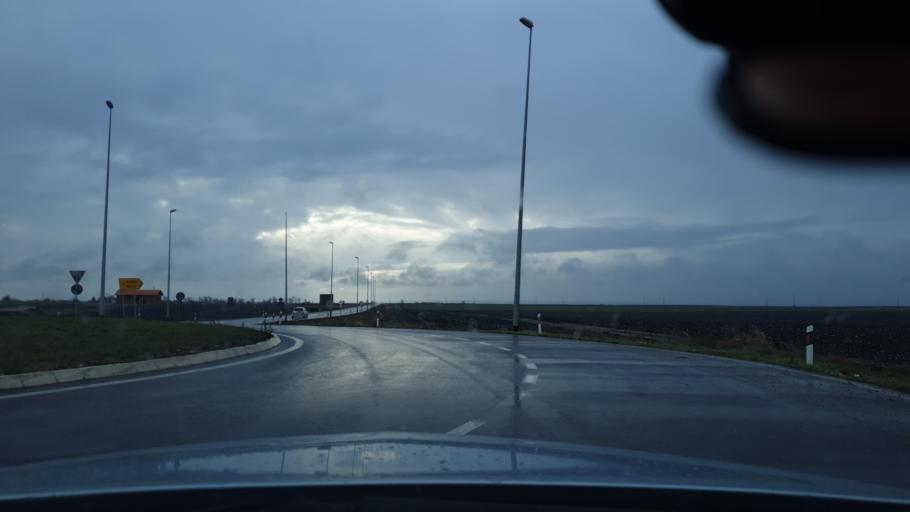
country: RS
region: Autonomna Pokrajina Vojvodina
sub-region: Juznobanatski Okrug
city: Kovin
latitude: 44.8240
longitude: 20.8513
